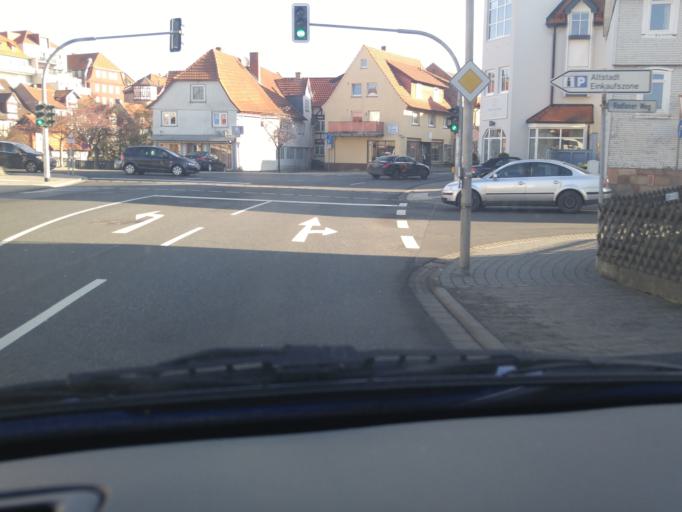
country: DE
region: Hesse
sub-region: Regierungsbezirk Giessen
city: Lauterbach
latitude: 50.6350
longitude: 9.3970
